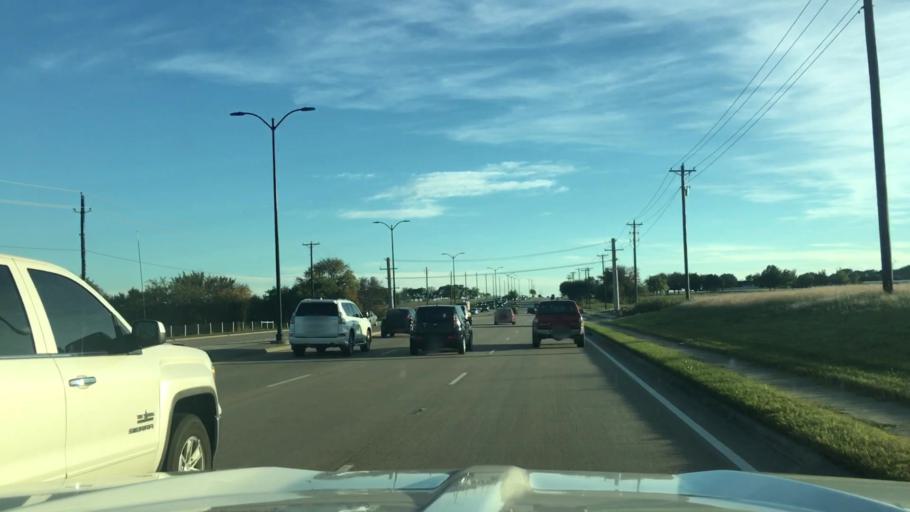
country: US
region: Texas
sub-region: Collin County
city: Frisco
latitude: 33.1721
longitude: -96.8032
